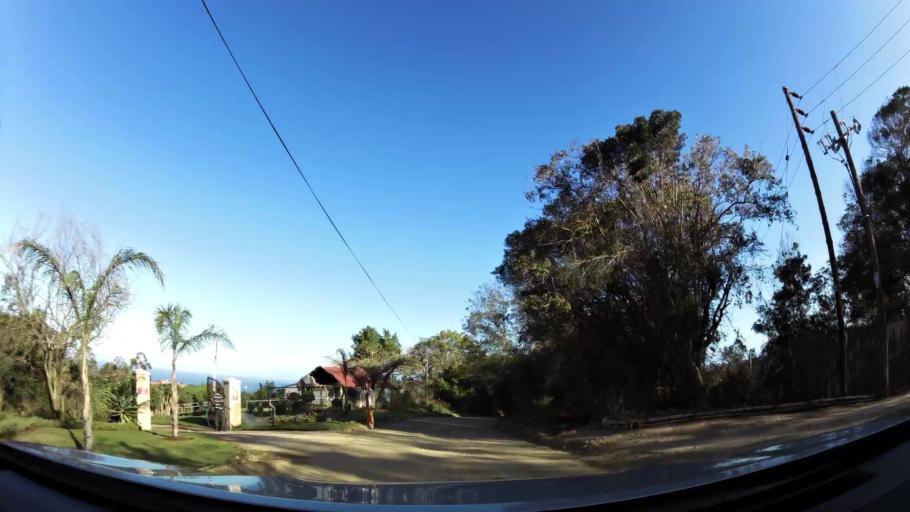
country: ZA
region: Western Cape
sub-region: Eden District Municipality
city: George
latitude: -33.9855
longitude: 22.5683
